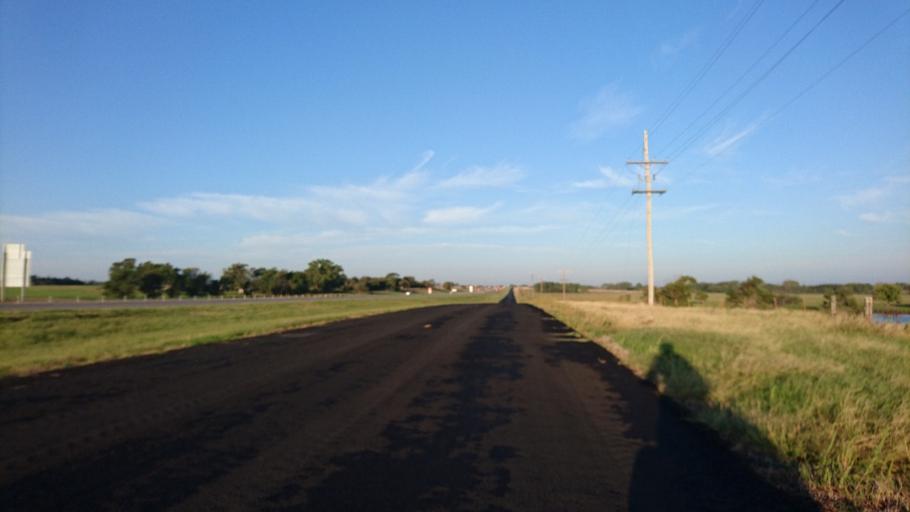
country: US
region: Oklahoma
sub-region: Beckham County
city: Sayre
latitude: 35.2624
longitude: -99.6836
